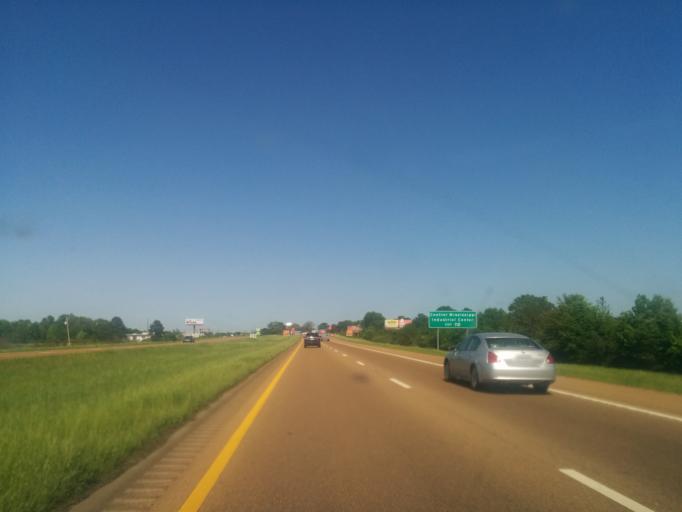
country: US
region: Mississippi
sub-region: Madison County
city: Madison
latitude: 32.5067
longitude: -90.1137
